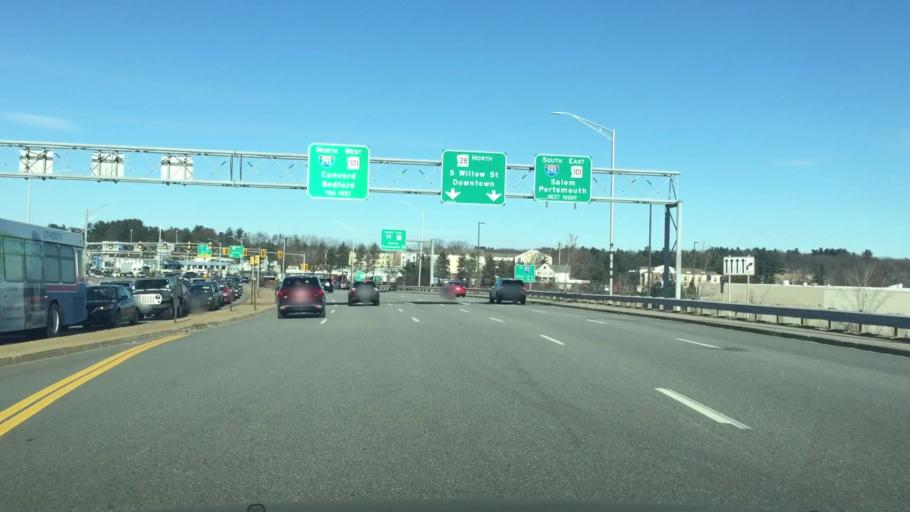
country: US
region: New Hampshire
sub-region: Hillsborough County
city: Manchester
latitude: 42.9553
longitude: -71.4359
